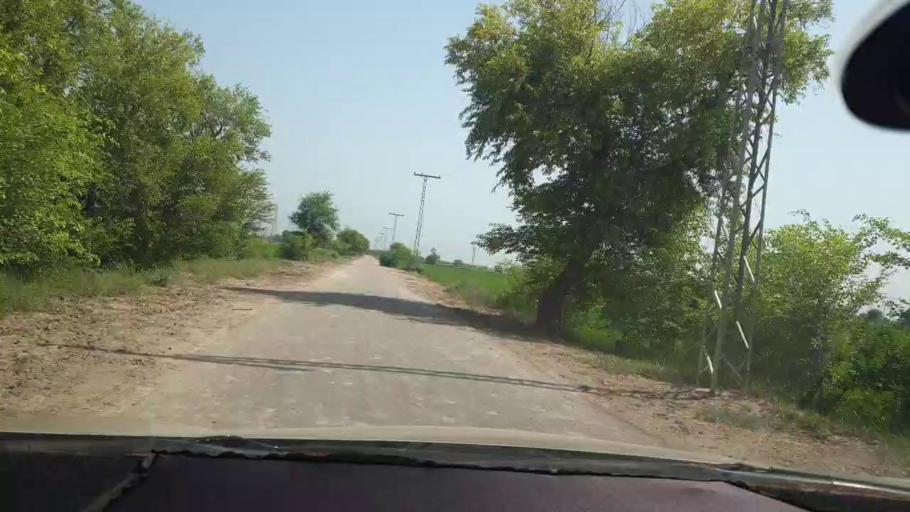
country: PK
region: Sindh
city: Kambar
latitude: 27.5021
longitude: 68.0162
